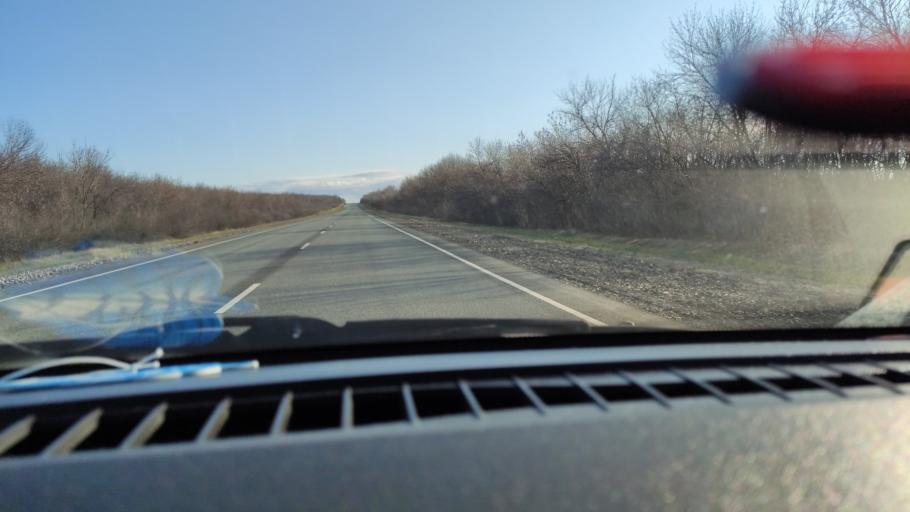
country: RU
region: Saratov
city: Khvalynsk
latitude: 52.6139
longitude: 48.1629
